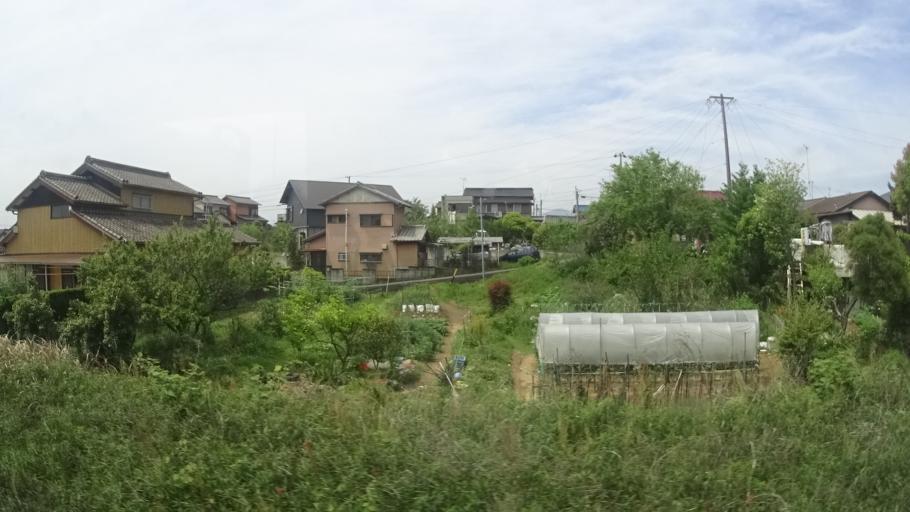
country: JP
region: Mie
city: Hisai-motomachi
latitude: 34.5628
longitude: 136.5469
